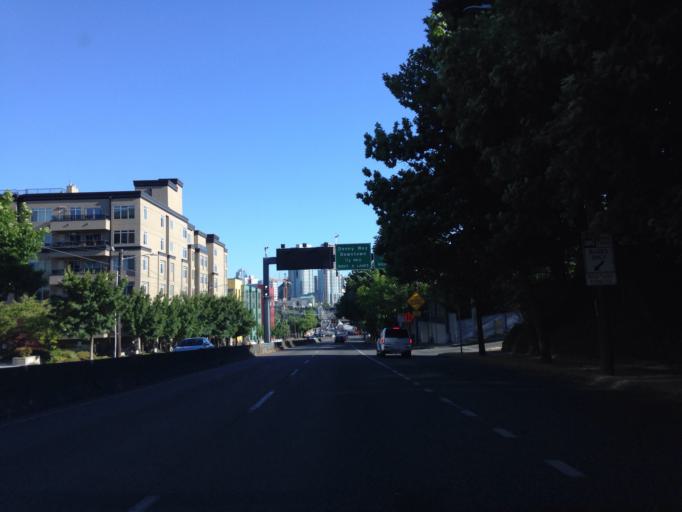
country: US
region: Washington
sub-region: King County
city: Seattle
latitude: 47.6285
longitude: -122.3436
